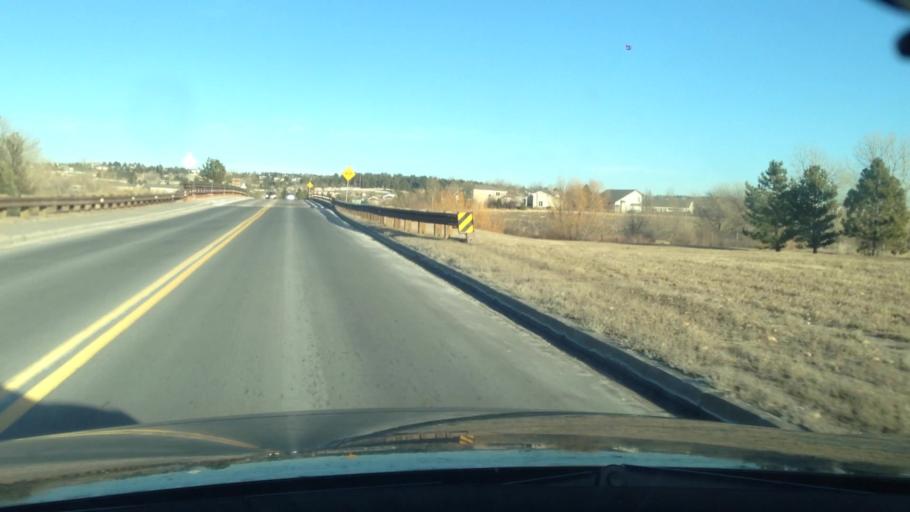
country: US
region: Colorado
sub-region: Douglas County
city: The Pinery
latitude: 39.4358
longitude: -104.7707
